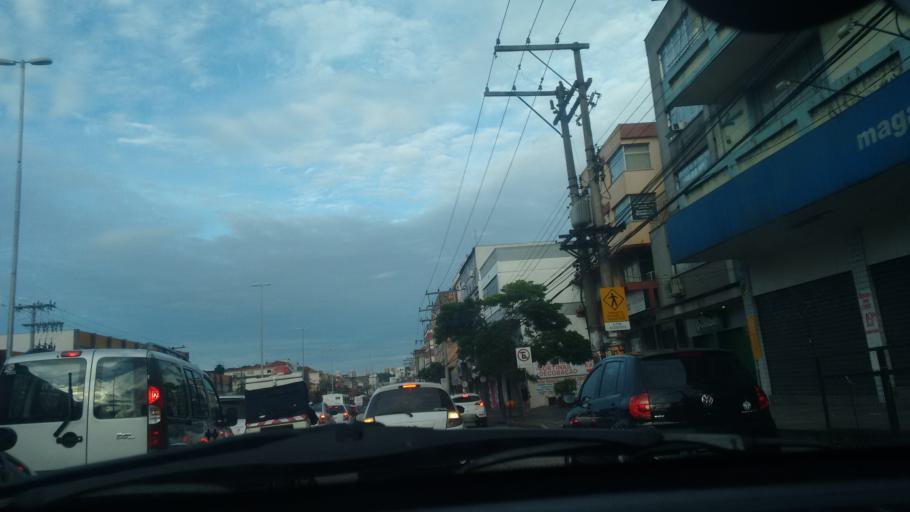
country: BR
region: Rio Grande do Sul
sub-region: Porto Alegre
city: Porto Alegre
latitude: -30.0110
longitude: -51.1624
